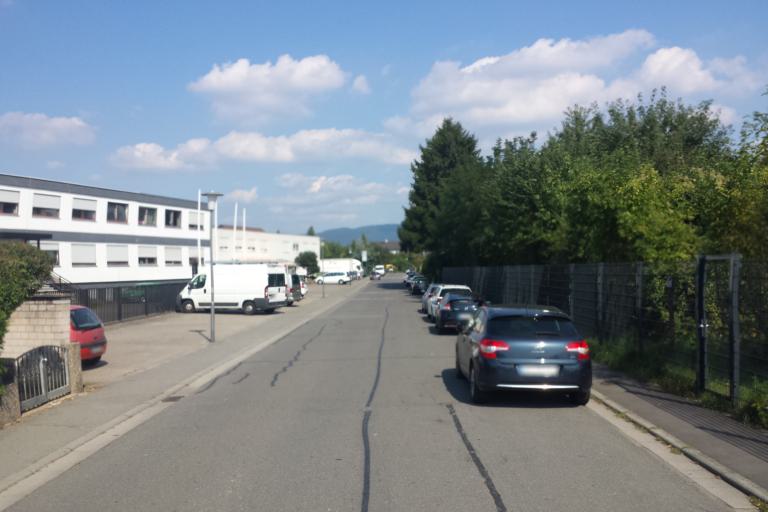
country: DE
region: Baden-Wuerttemberg
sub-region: Karlsruhe Region
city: Eppelheim
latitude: 49.4110
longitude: 8.6297
